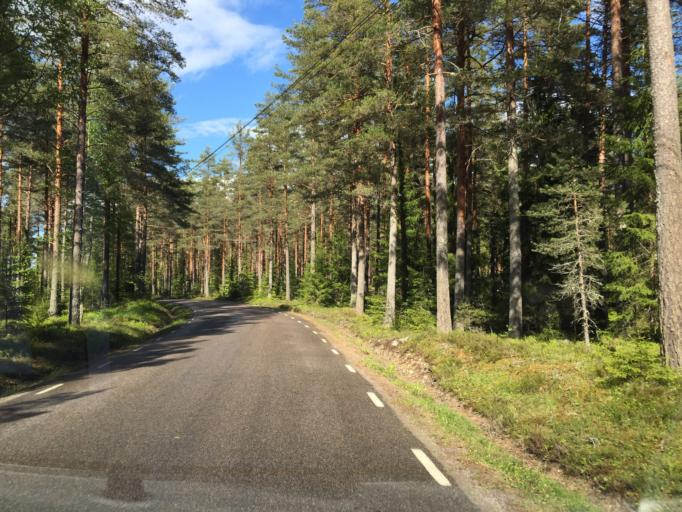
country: SE
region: Soedermanland
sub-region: Vingakers Kommun
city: Vingaker
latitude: 58.9738
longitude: 15.6800
